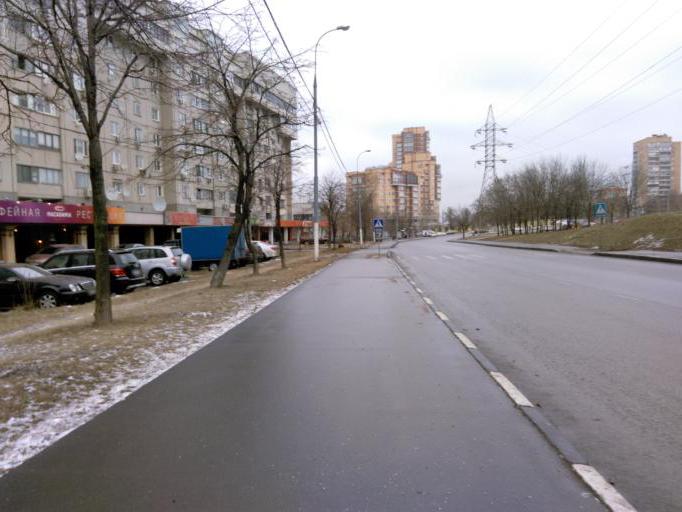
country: RU
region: Moskovskaya
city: Semenovskoye
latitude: 55.6720
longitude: 37.5428
